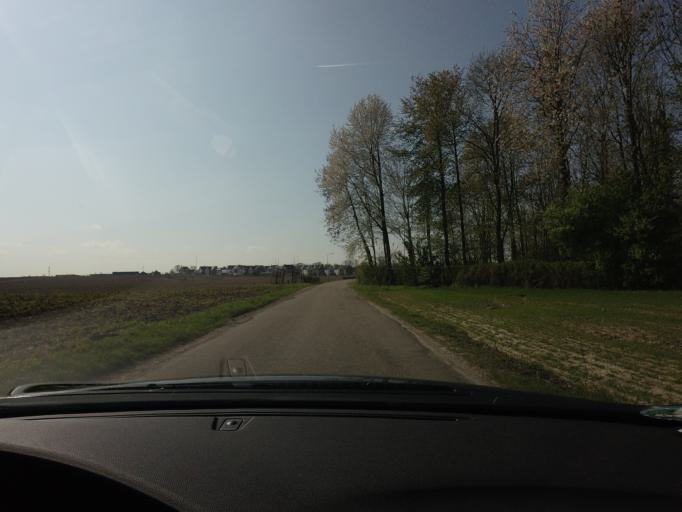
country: NL
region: Limburg
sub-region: Eijsden-Margraten
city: Margraten
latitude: 50.8279
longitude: 5.8271
